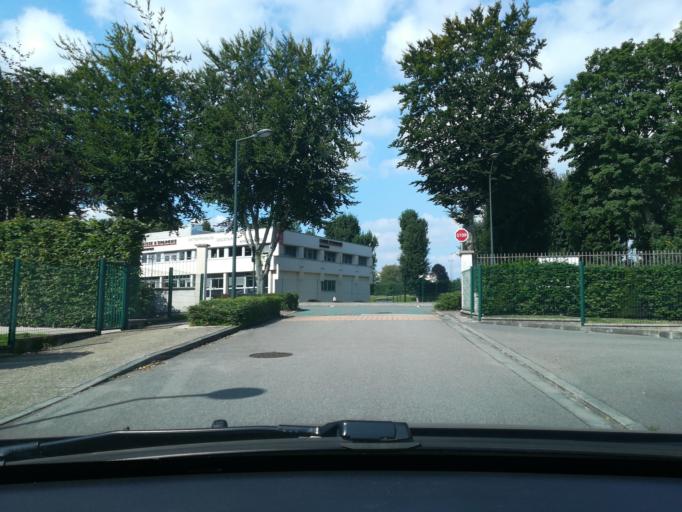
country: FR
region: Haute-Normandie
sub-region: Departement de la Seine-Maritime
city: Bois-Guillaume
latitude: 49.4693
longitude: 1.1229
